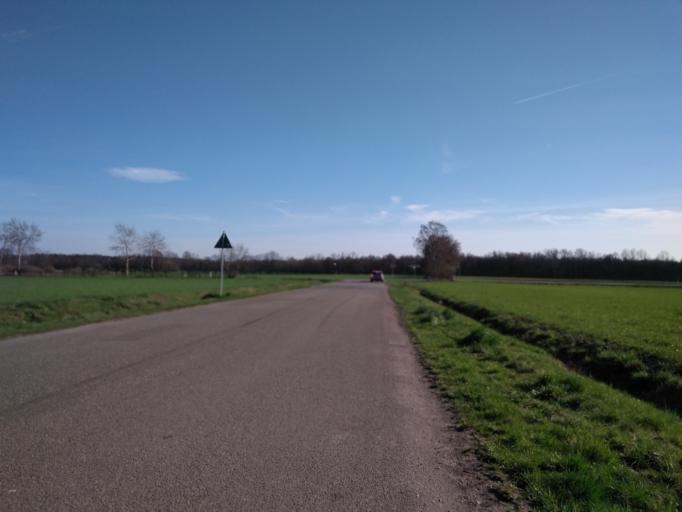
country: DE
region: North Rhine-Westphalia
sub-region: Regierungsbezirk Dusseldorf
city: Hunxe
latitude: 51.6090
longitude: 6.8457
